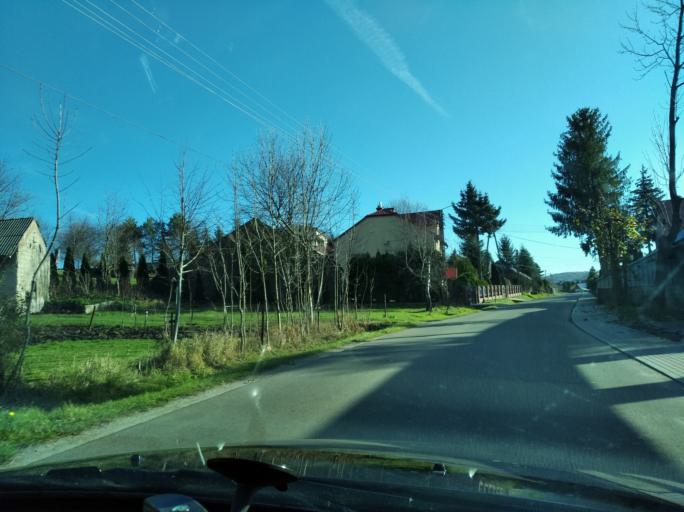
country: PL
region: Subcarpathian Voivodeship
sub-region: Powiat rzeszowski
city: Lutoryz
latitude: 49.9668
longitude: 21.9129
